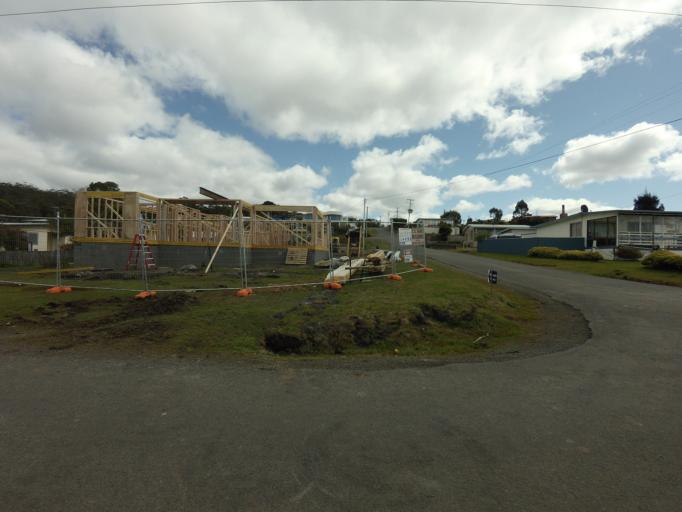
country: AU
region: Tasmania
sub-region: Huon Valley
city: Geeveston
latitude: -43.4394
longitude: 146.9614
